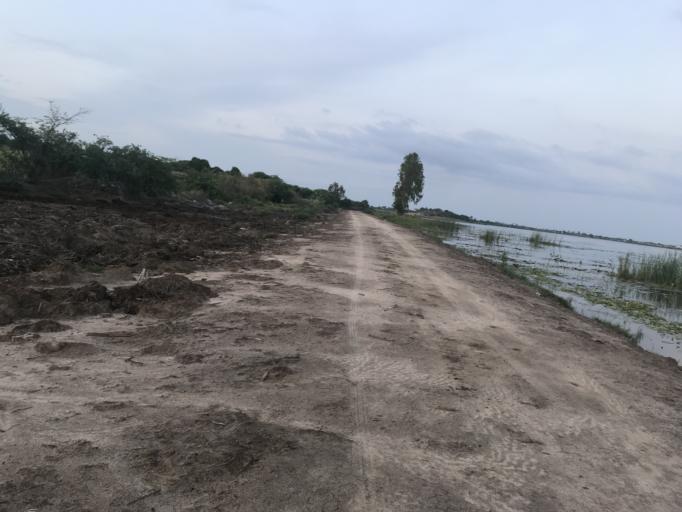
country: SN
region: Saint-Louis
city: Saint-Louis
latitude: 16.0491
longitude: -16.4137
